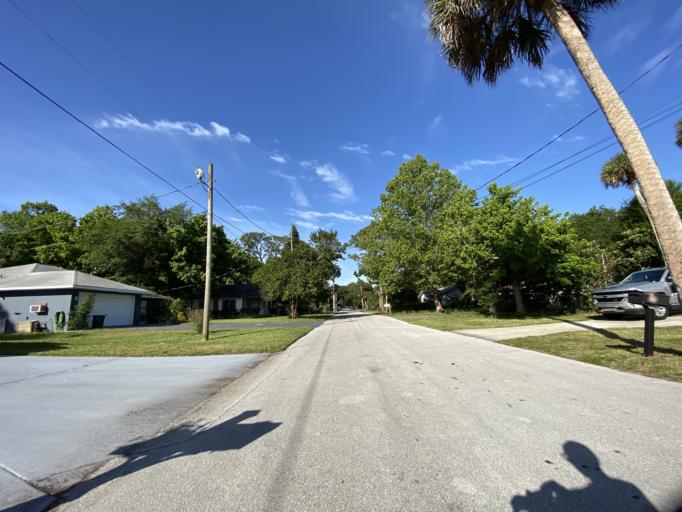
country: US
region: Florida
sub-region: Volusia County
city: South Daytona
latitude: 29.1785
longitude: -81.0183
